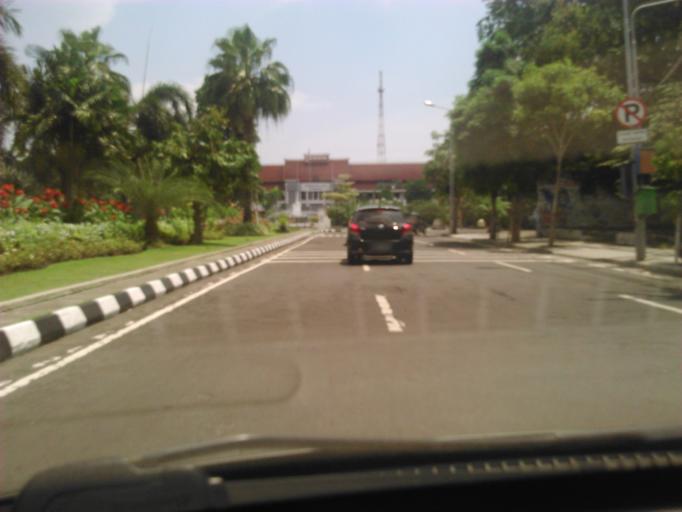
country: ID
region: East Java
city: Pacarkeling
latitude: -7.2615
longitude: 112.7466
